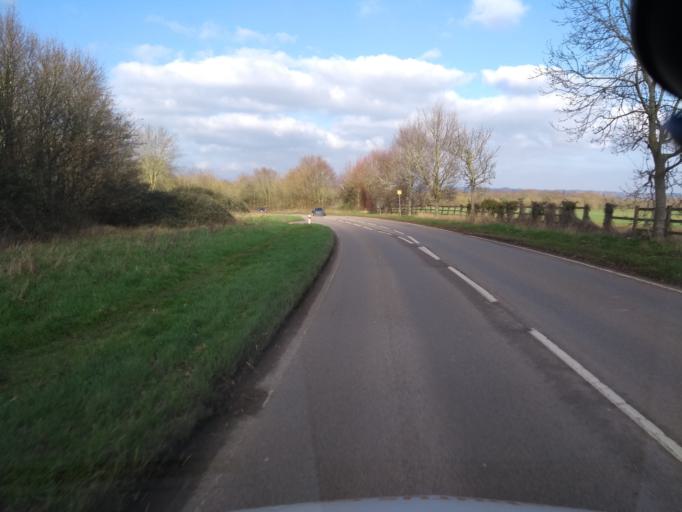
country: GB
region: England
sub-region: Somerset
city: Taunton
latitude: 50.9956
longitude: -3.0816
